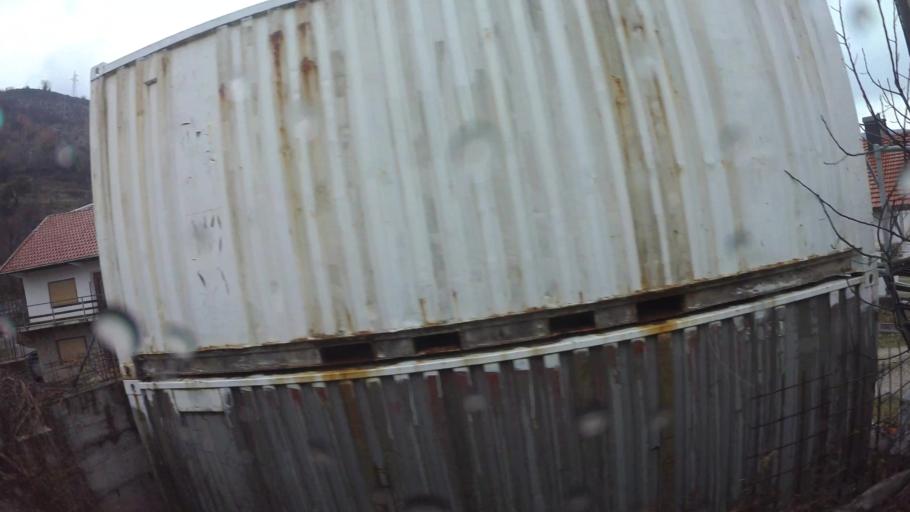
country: BA
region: Federation of Bosnia and Herzegovina
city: Cim
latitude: 43.3551
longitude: 17.7819
